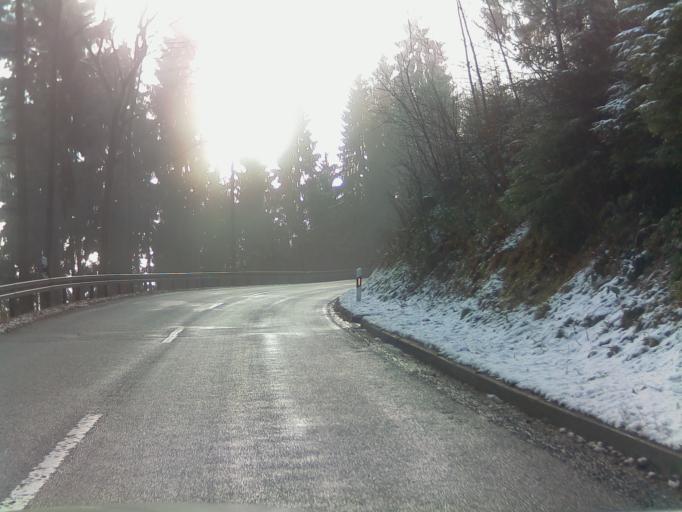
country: DE
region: Thuringia
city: Frankenhain
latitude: 50.7630
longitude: 10.7696
